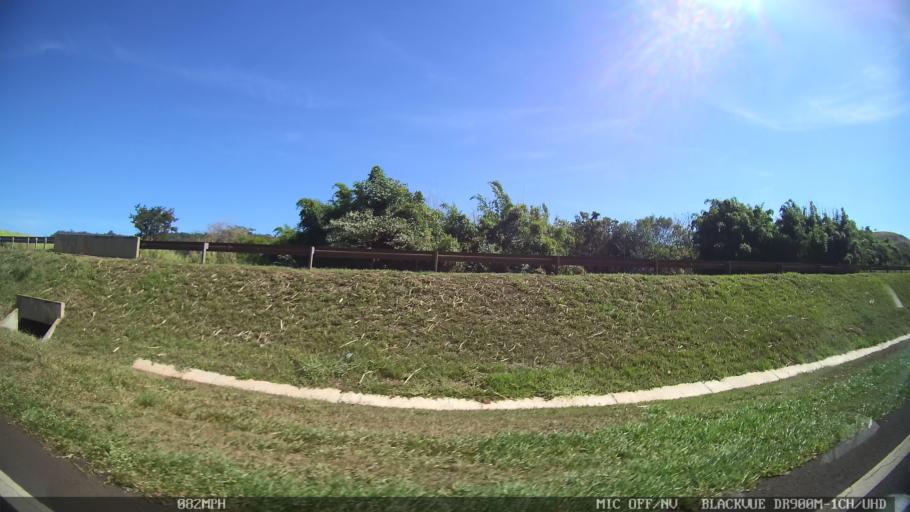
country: BR
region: Sao Paulo
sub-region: Sao Simao
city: Sao Simao
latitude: -21.4890
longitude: -47.6411
